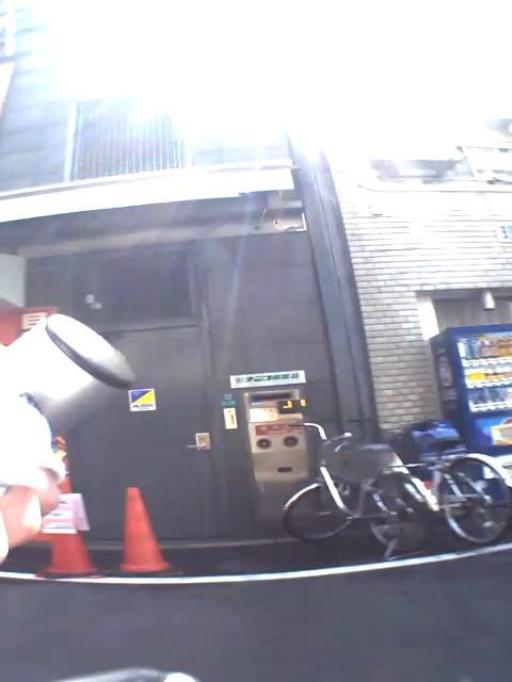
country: JP
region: Osaka
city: Osaka-shi
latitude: 34.6626
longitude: 135.5050
